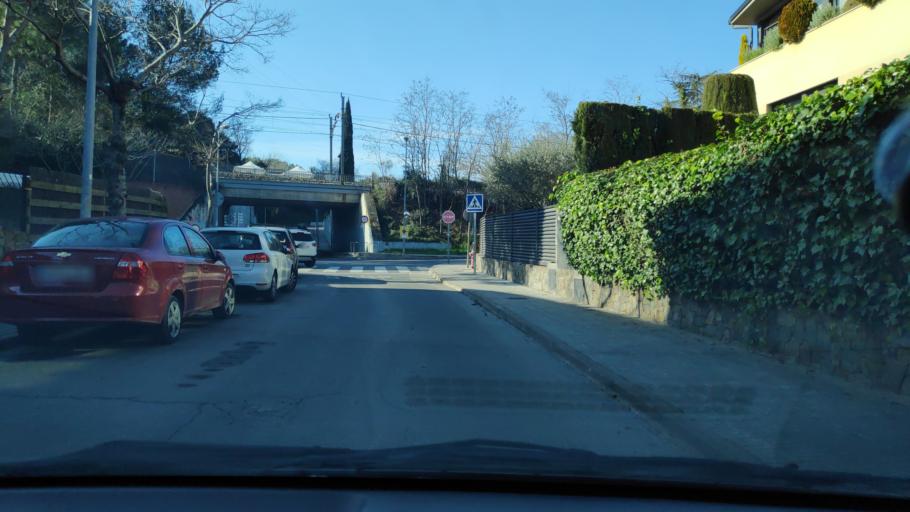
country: ES
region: Catalonia
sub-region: Provincia de Barcelona
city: Sant Cugat del Valles
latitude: 41.4571
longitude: 2.0691
